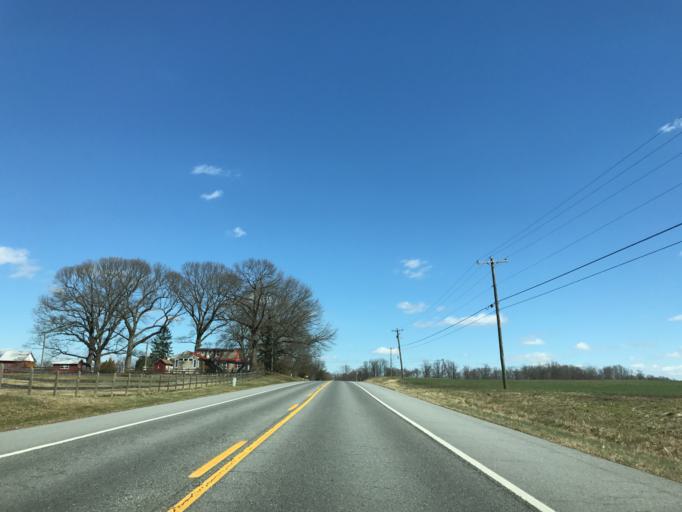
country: US
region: Maryland
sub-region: Queen Anne's County
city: Kingstown
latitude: 39.2411
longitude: -75.8856
